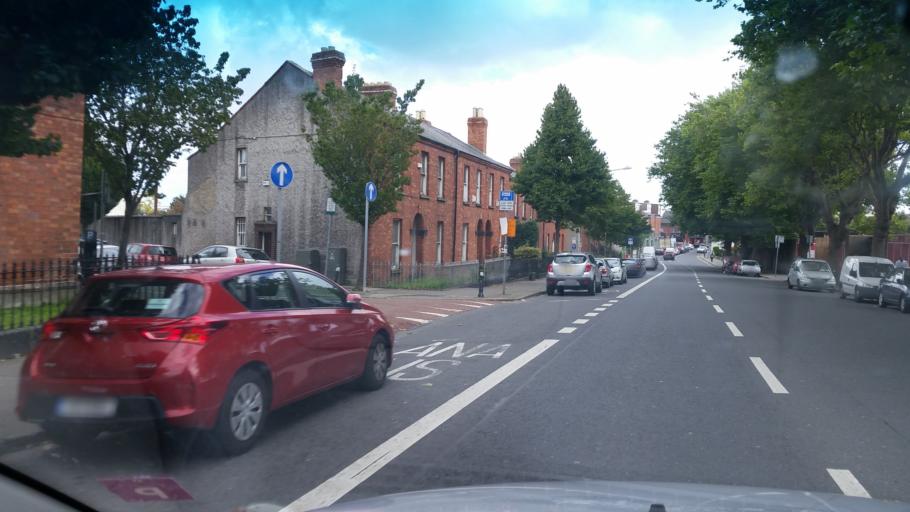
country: IE
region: Leinster
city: Rathgar
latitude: 53.3318
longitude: -6.2782
